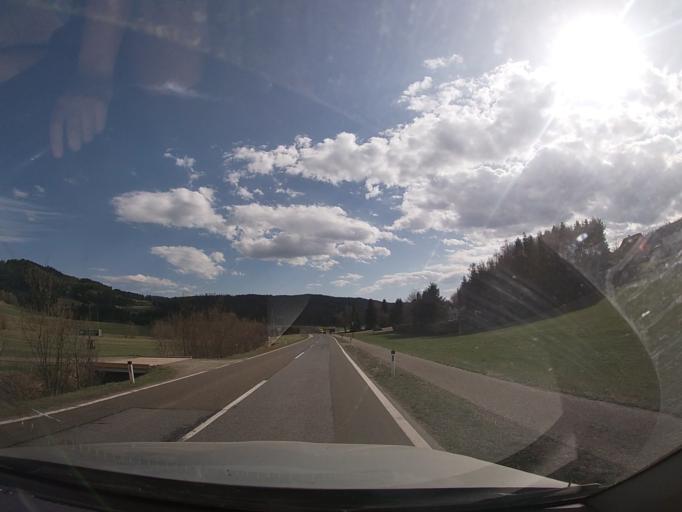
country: AT
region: Styria
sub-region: Politischer Bezirk Murau
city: Perchau am Sattel
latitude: 47.1052
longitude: 14.4563
